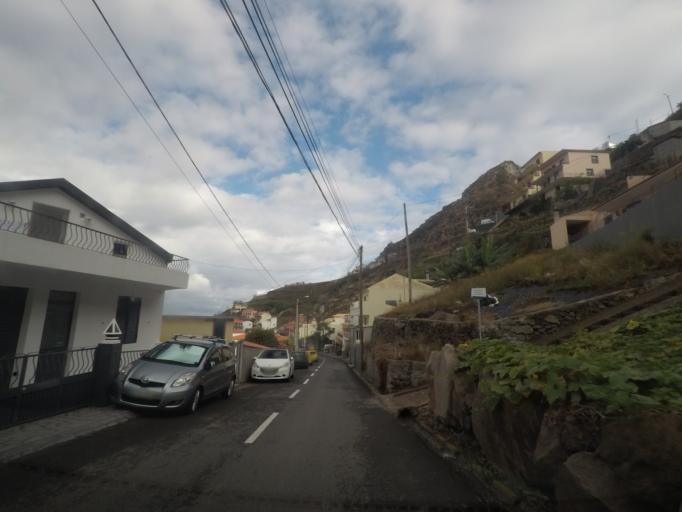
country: PT
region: Madeira
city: Camara de Lobos
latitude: 32.6564
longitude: -16.9963
